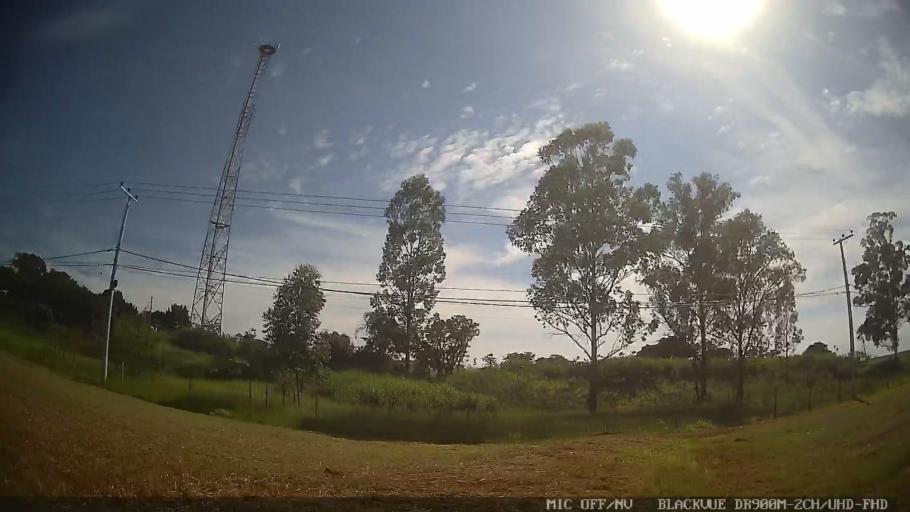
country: BR
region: Sao Paulo
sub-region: Porto Feliz
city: Porto Feliz
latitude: -23.3441
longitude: -47.5276
